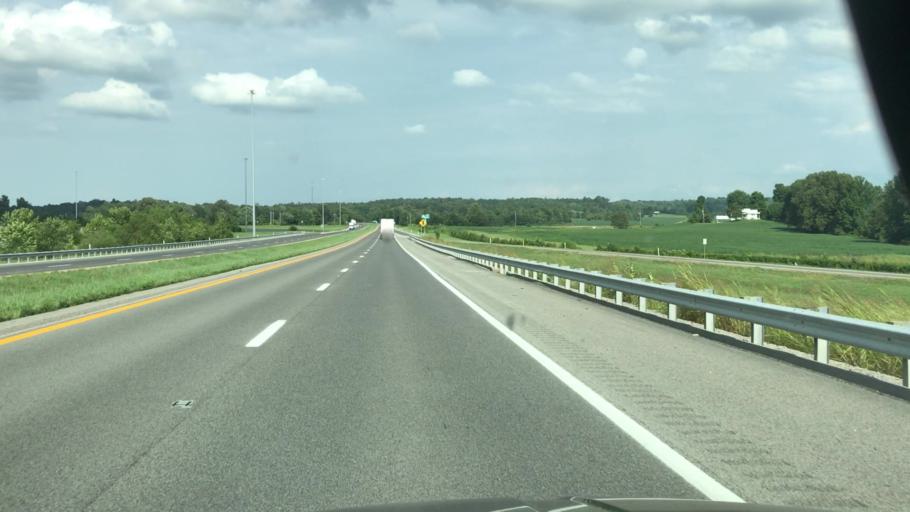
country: US
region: Kentucky
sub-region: Muhlenberg County
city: Greenville
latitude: 37.2348
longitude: -87.2723
